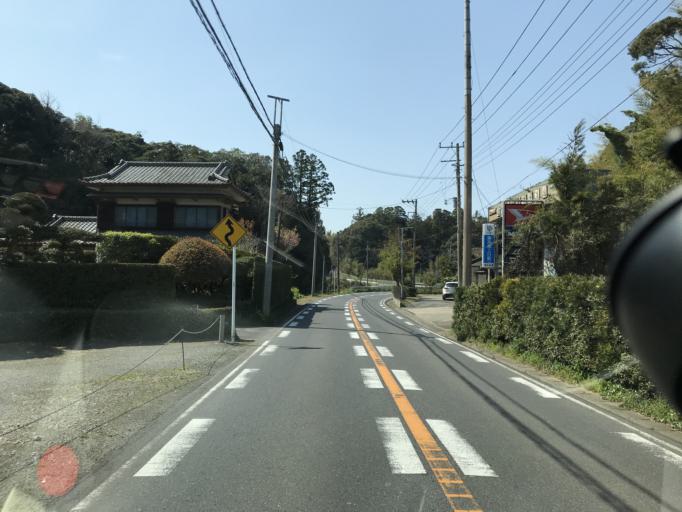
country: JP
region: Chiba
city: Yokaichiba
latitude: 35.7565
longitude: 140.5830
